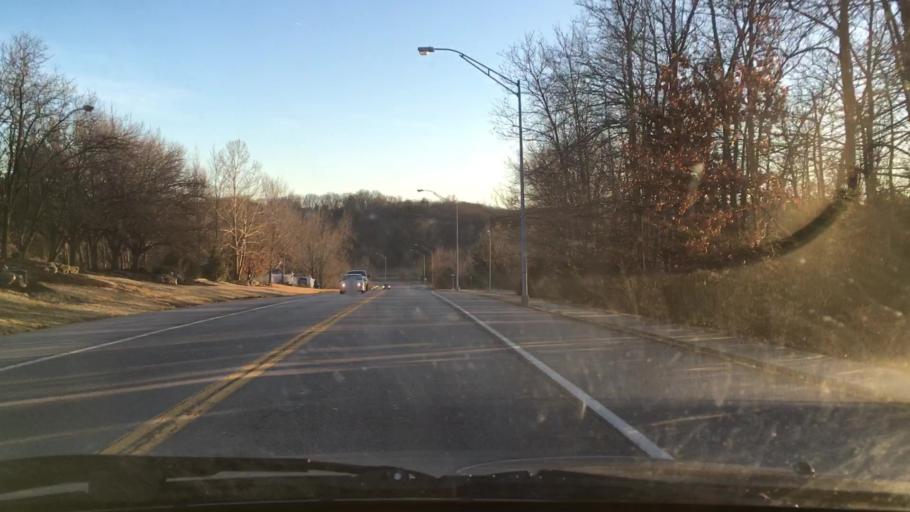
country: US
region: Missouri
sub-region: Boone County
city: Columbia
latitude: 38.9257
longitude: -92.3648
